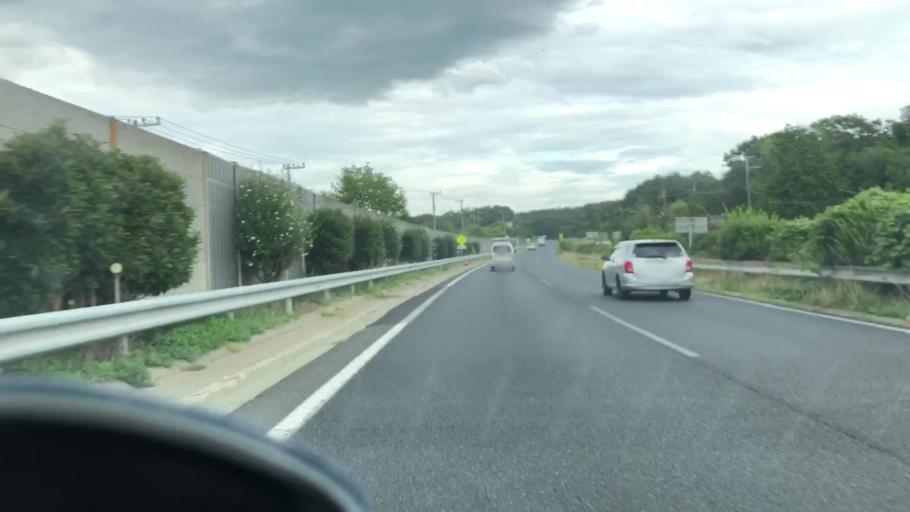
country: JP
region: Hyogo
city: Yashiro
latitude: 34.9173
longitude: 135.0205
